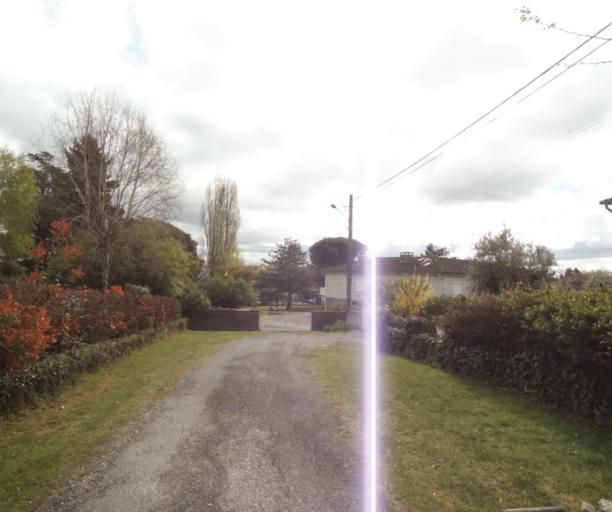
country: FR
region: Midi-Pyrenees
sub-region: Departement de l'Ariege
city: Saverdun
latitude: 43.2316
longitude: 1.5700
